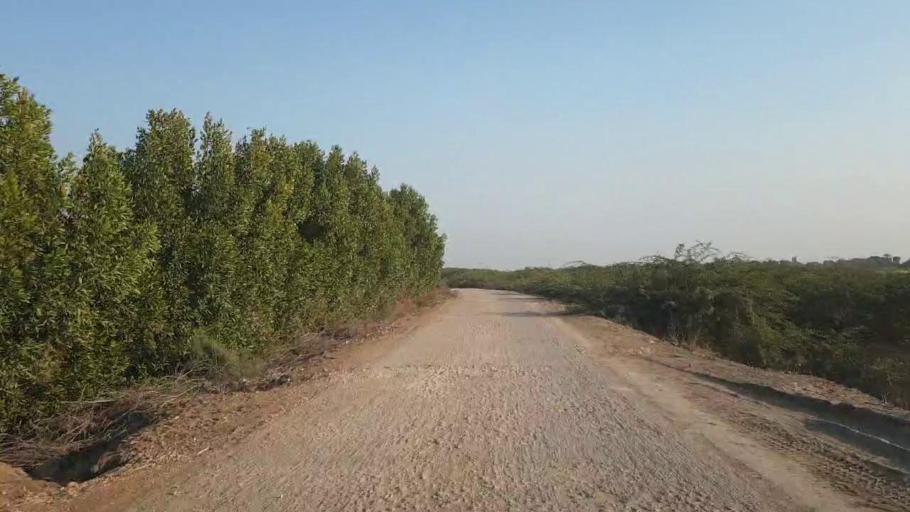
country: PK
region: Sindh
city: Mirpur Khas
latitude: 25.4232
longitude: 68.9053
